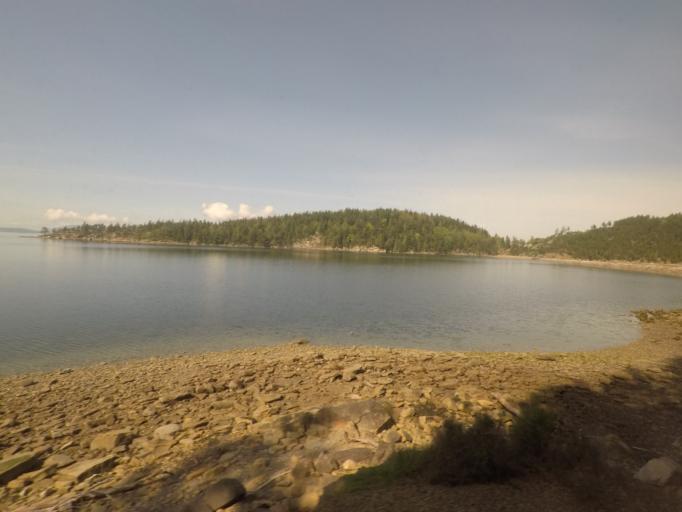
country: US
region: Washington
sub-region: Whatcom County
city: Bellingham
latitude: 48.6950
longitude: -122.4962
